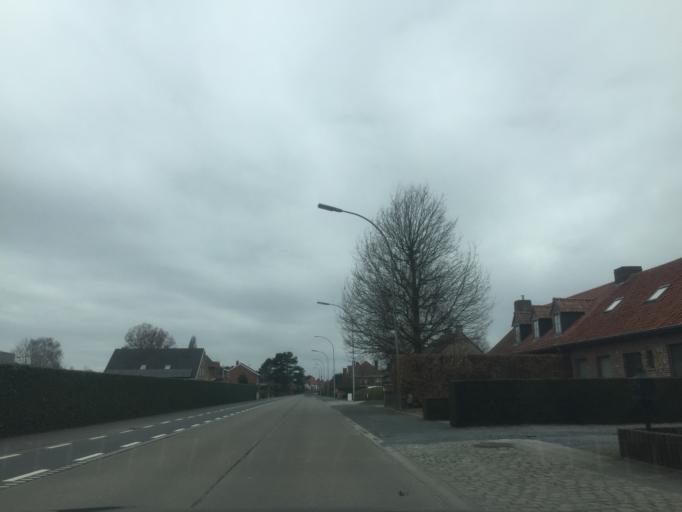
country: BE
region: Flanders
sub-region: Provincie West-Vlaanderen
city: Izegem
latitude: 50.9292
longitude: 3.2088
